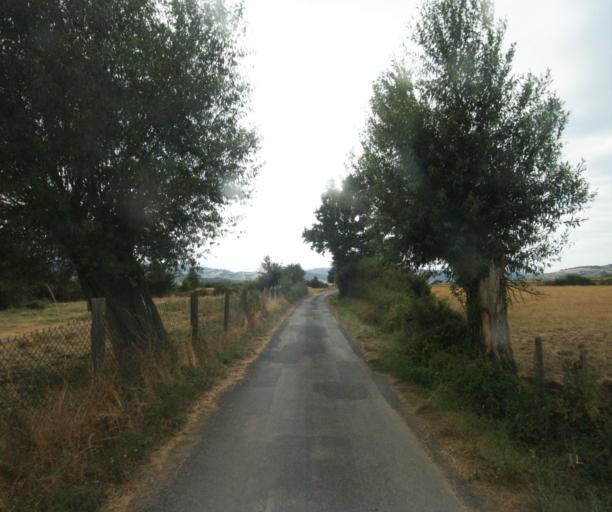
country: FR
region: Rhone-Alpes
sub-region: Departement du Rhone
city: Saint-Verand
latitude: 45.8846
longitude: 4.5474
